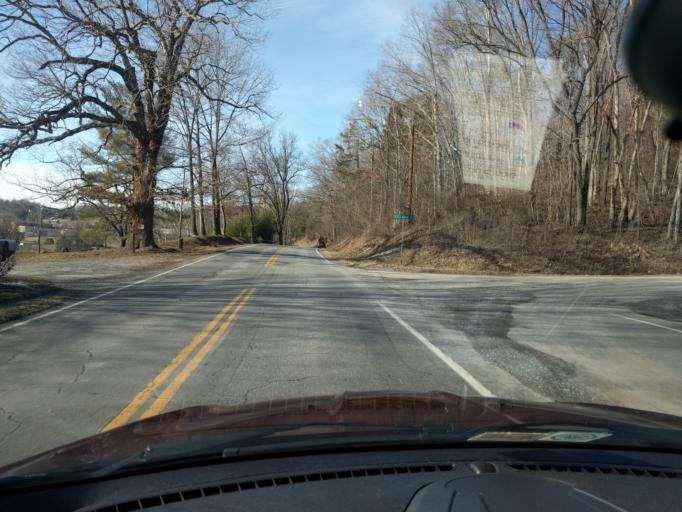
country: US
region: Virginia
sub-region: Botetourt County
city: Buchanan
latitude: 37.5433
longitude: -79.7184
